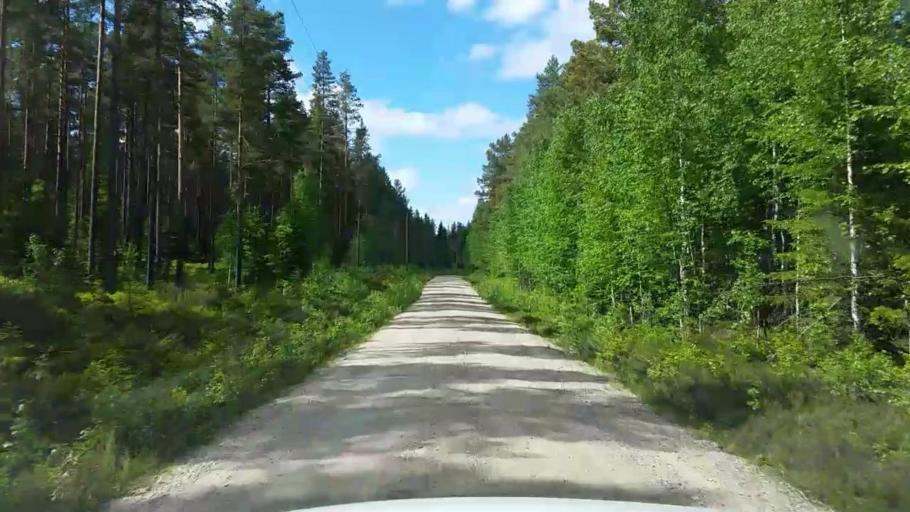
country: SE
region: Gaevleborg
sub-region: Ovanakers Kommun
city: Alfta
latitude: 61.5470
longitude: 15.9690
